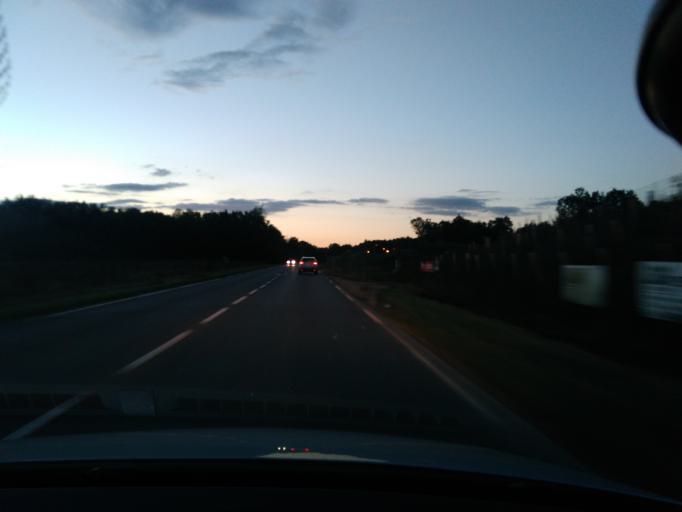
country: FR
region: Ile-de-France
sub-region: Departement de Seine-et-Marne
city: Villeneuve-le-Comte
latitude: 48.8212
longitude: 2.8147
